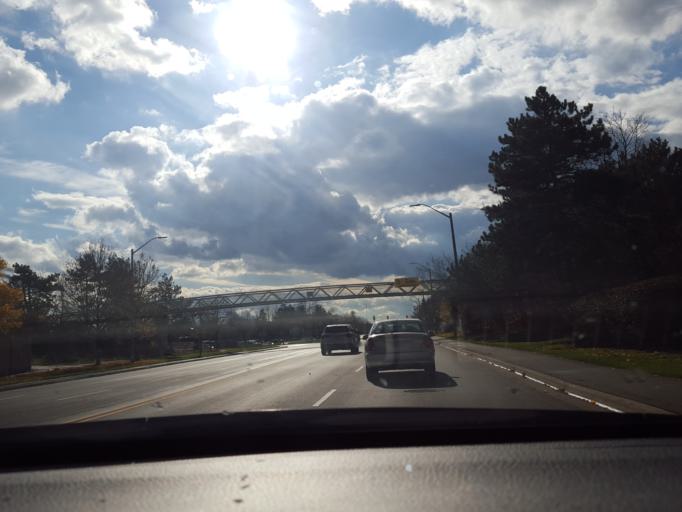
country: CA
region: Ontario
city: Brampton
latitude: 43.5946
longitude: -79.7642
